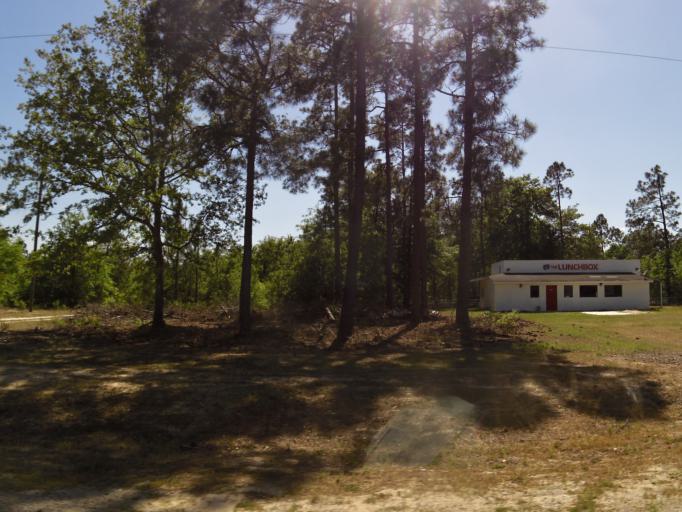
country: US
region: South Carolina
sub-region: Barnwell County
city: Williston
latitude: 33.4667
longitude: -81.5034
